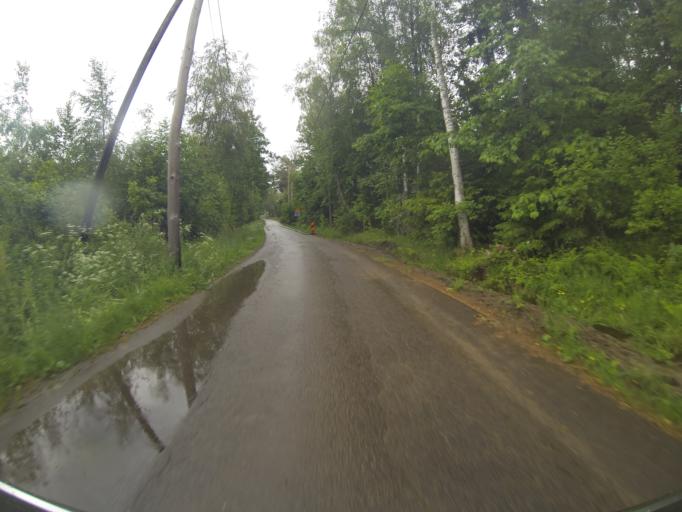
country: SE
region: Blekinge
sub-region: Ronneby Kommun
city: Ronneby
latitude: 56.1703
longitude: 15.3123
